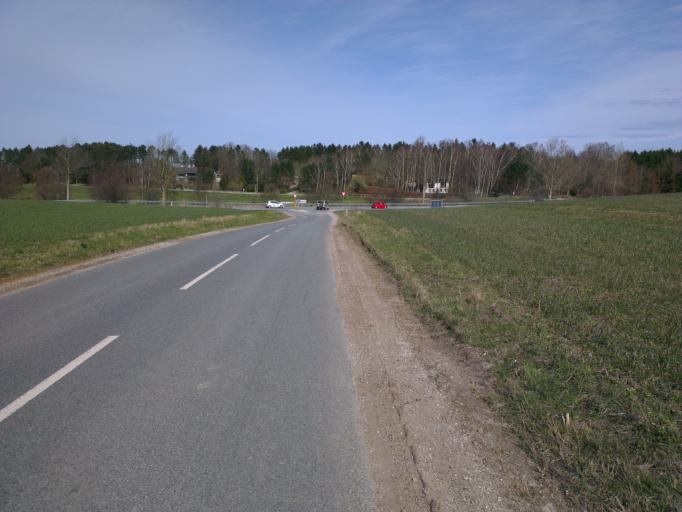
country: DK
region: Capital Region
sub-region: Frederikssund Kommune
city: Frederikssund
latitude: 55.8459
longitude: 12.1254
